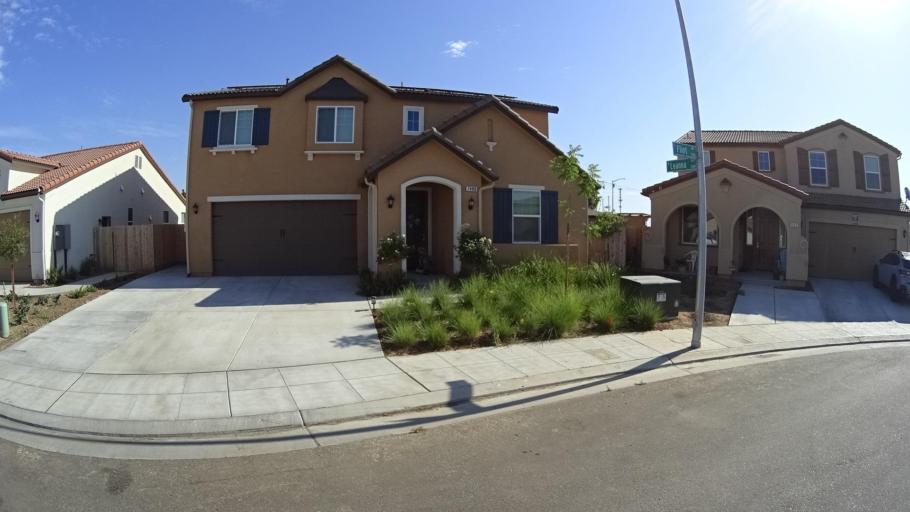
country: US
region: California
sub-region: Fresno County
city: Tarpey Village
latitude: 36.7873
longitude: -119.6558
